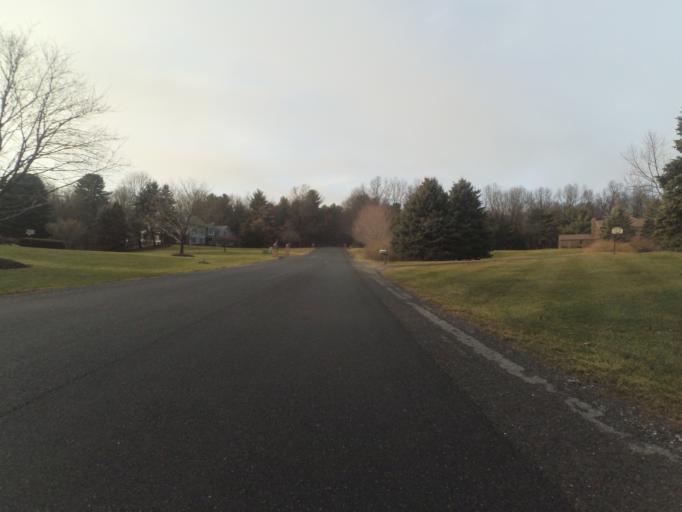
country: US
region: Pennsylvania
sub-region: Centre County
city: Park Forest Village
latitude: 40.7813
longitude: -77.9198
